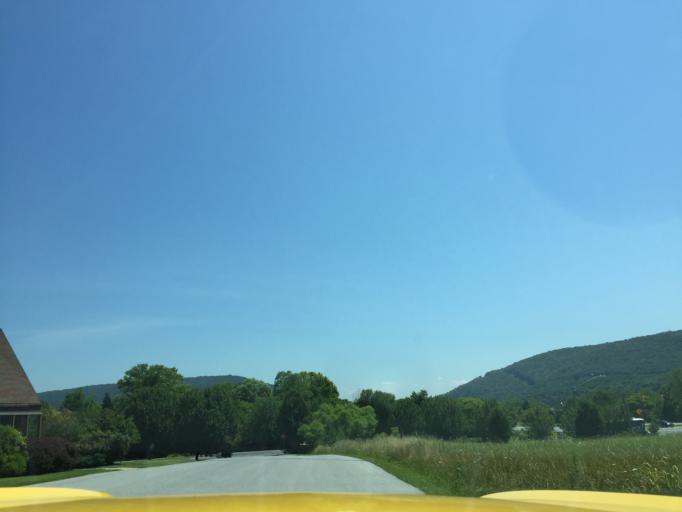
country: US
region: West Virginia
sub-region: Jefferson County
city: Bolivar
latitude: 39.3195
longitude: -77.7606
